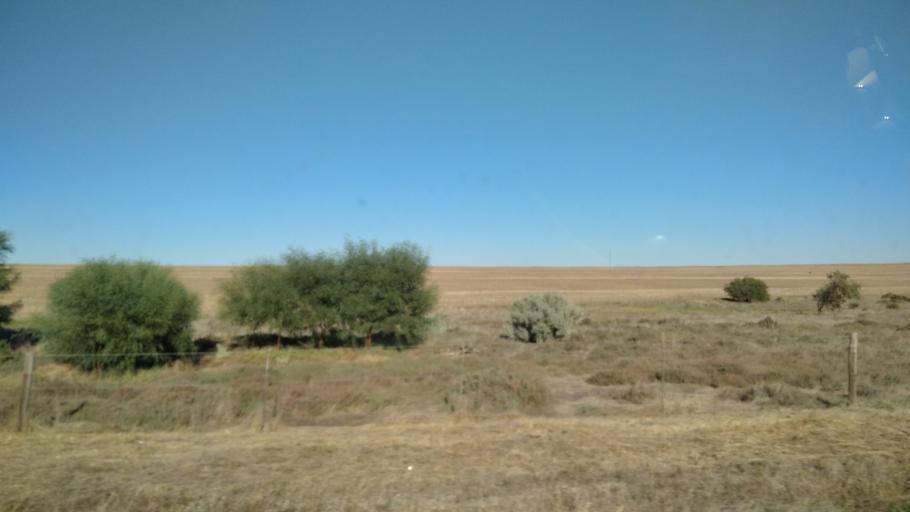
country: ZA
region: Western Cape
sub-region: West Coast District Municipality
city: Malmesbury
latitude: -33.3474
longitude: 18.6397
